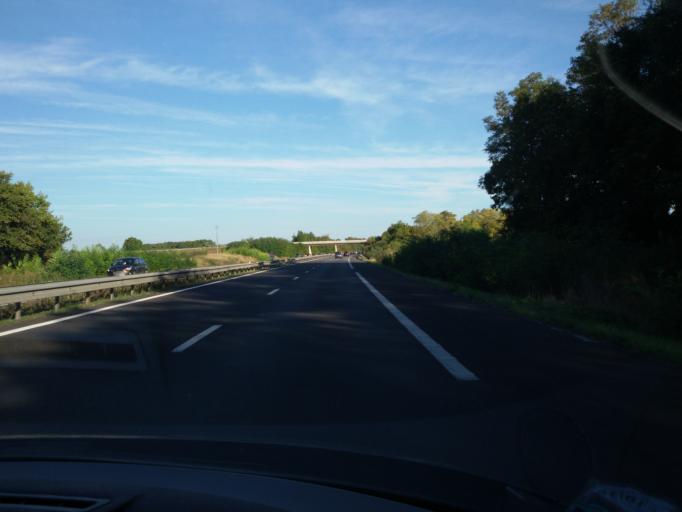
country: FR
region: Centre
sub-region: Departement du Cher
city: Mehun-sur-Yevre
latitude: 47.1099
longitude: 2.2053
